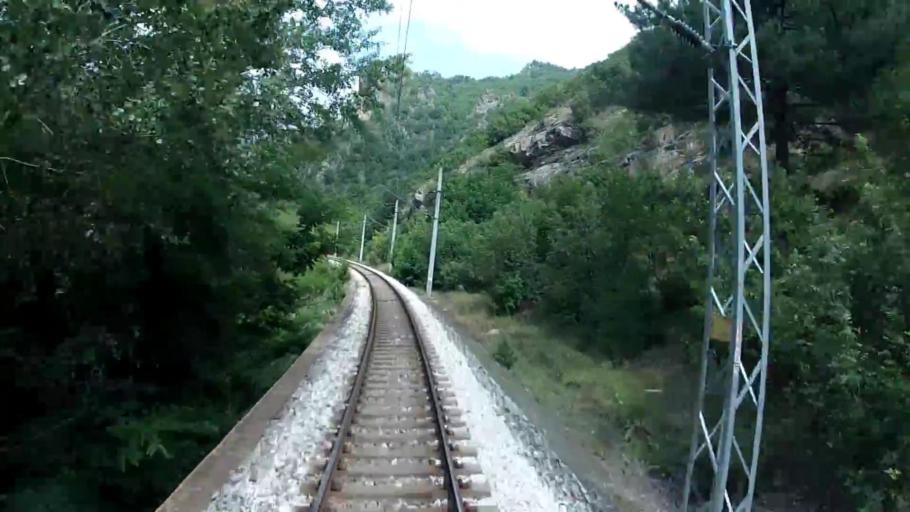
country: BG
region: Blagoevgrad
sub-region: Obshtina Kresna
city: Stara Kresna
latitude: 41.8261
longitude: 23.1534
